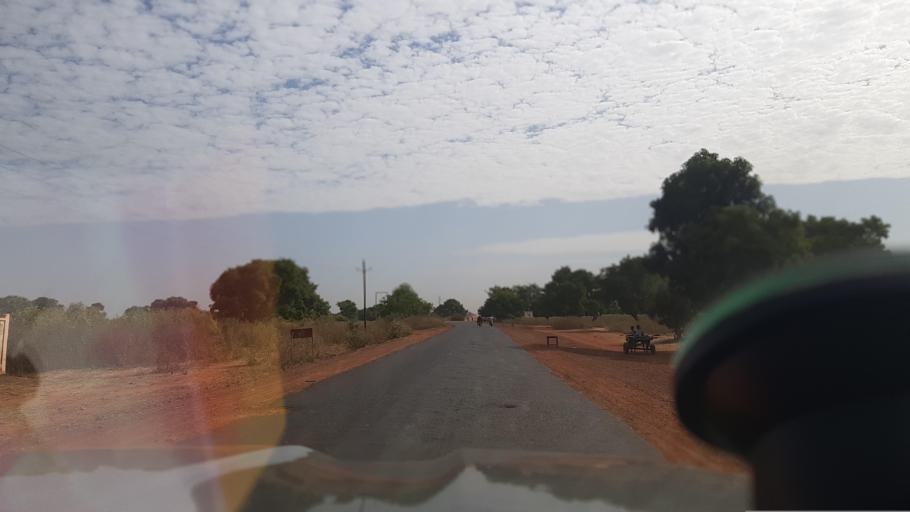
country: ML
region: Segou
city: Segou
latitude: 13.4992
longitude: -6.1551
